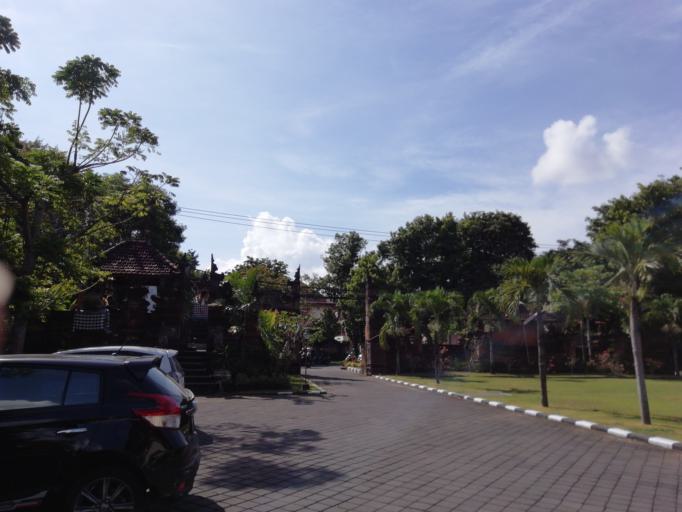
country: ID
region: Bali
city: Denpasar
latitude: -8.6714
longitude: 115.2213
